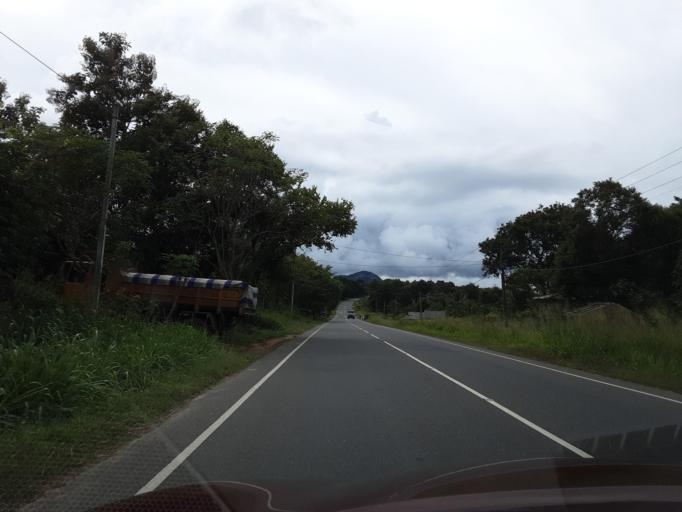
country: LK
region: Uva
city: Badulla
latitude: 7.3876
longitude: 81.1474
